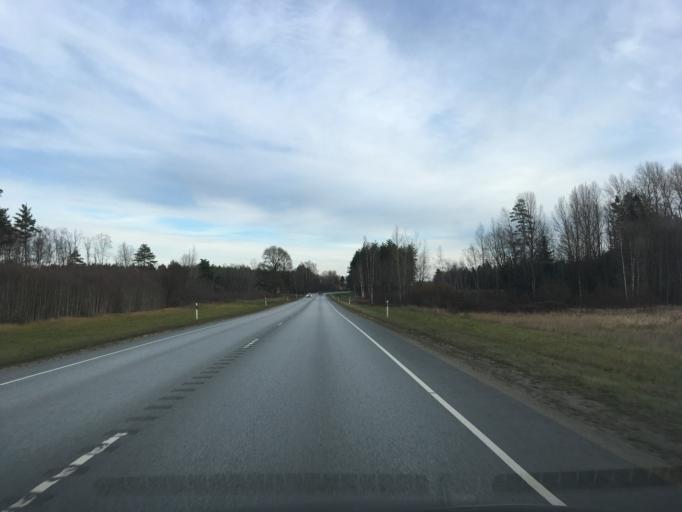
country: EE
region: Laeaene-Virumaa
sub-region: Viru-Nigula vald
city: Kunda
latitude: 59.4044
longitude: 26.6349
